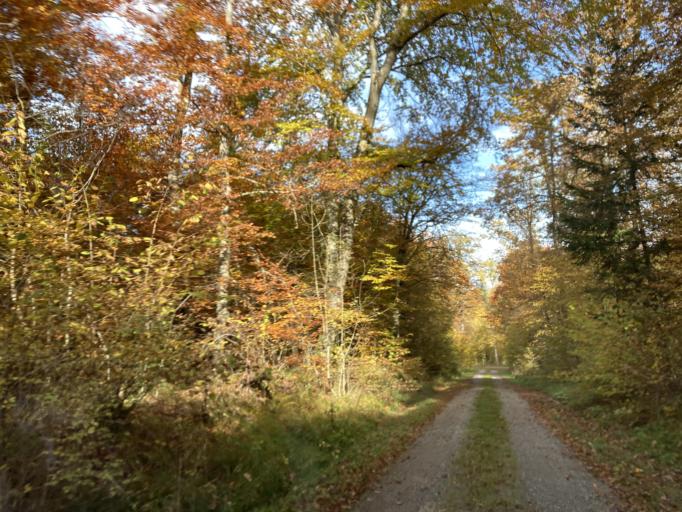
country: DE
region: Baden-Wuerttemberg
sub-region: Tuebingen Region
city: Rottenburg
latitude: 48.4392
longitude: 8.9668
